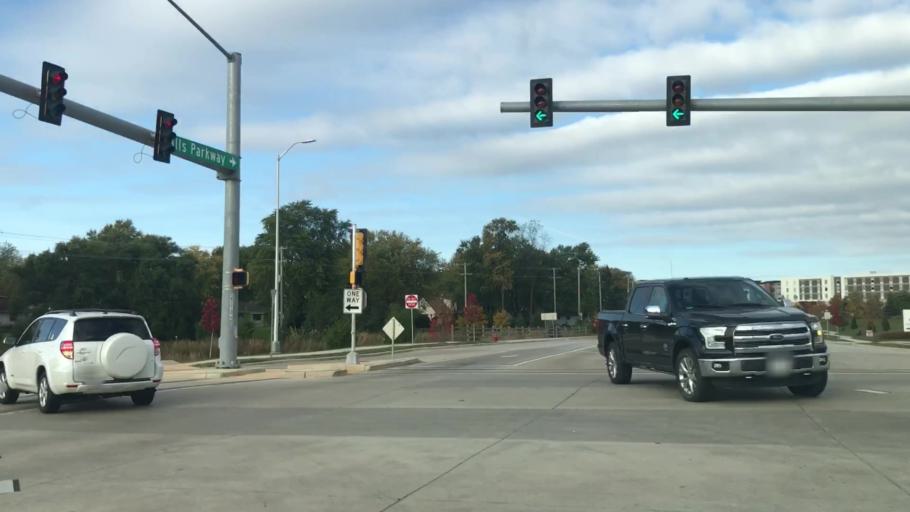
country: US
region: Wisconsin
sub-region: Waukesha County
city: Menomonee Falls
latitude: 43.1811
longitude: -88.1030
